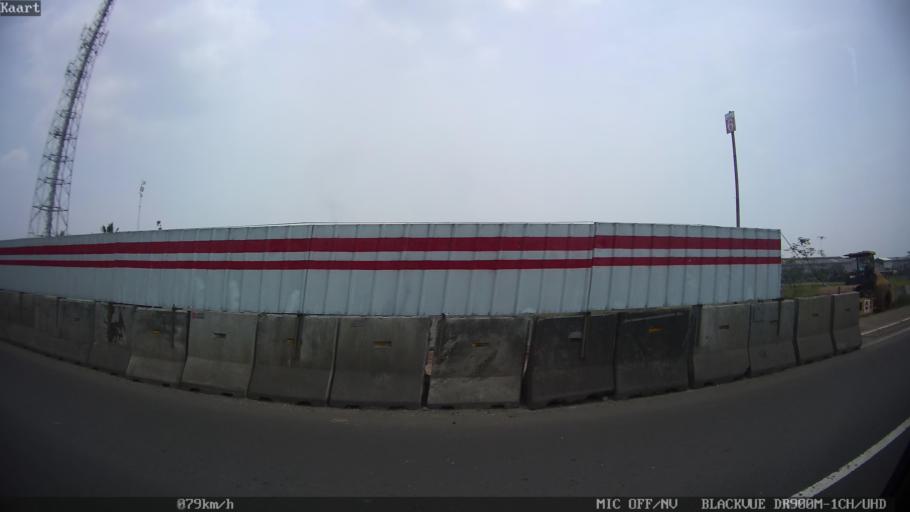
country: ID
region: West Java
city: Kresek
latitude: -6.1645
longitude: 106.3334
